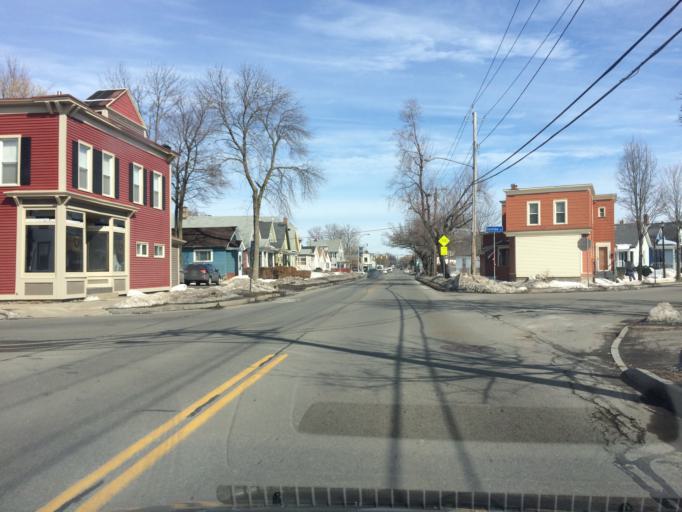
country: US
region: New York
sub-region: Monroe County
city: Rochester
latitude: 43.1380
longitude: -77.5971
